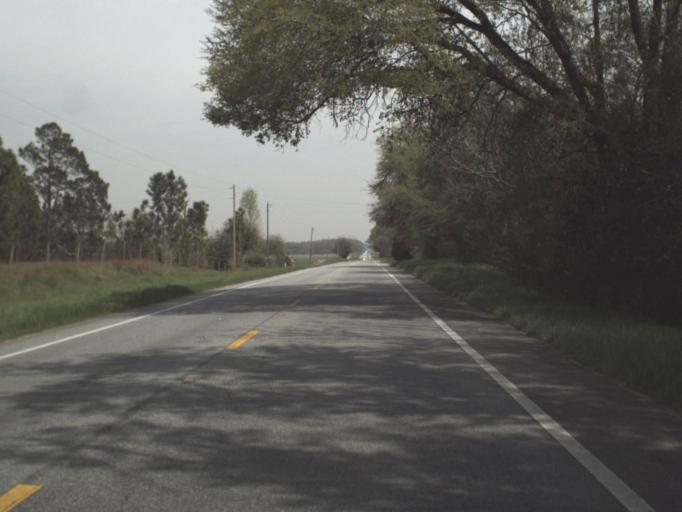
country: US
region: Florida
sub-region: Jackson County
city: Malone
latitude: 30.9755
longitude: -85.0772
